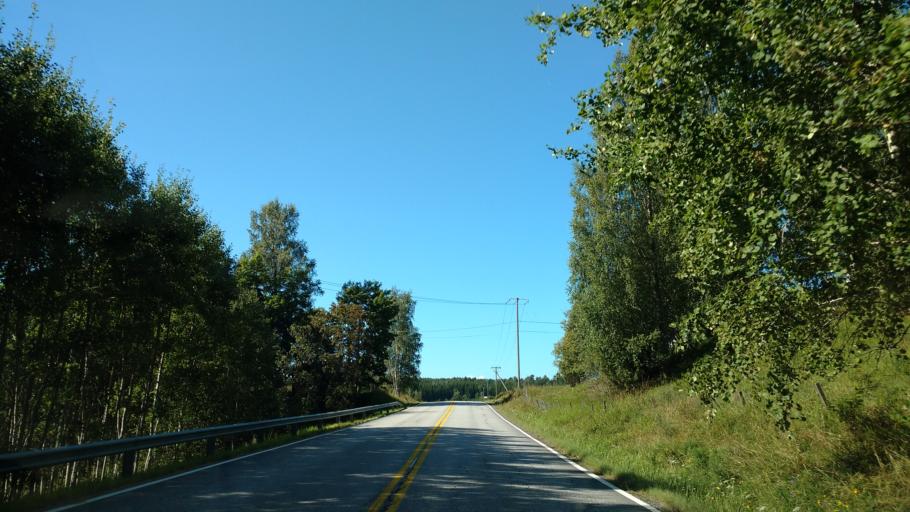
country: FI
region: Uusimaa
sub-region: Raaseporin
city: Pohja
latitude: 60.1442
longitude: 23.5549
